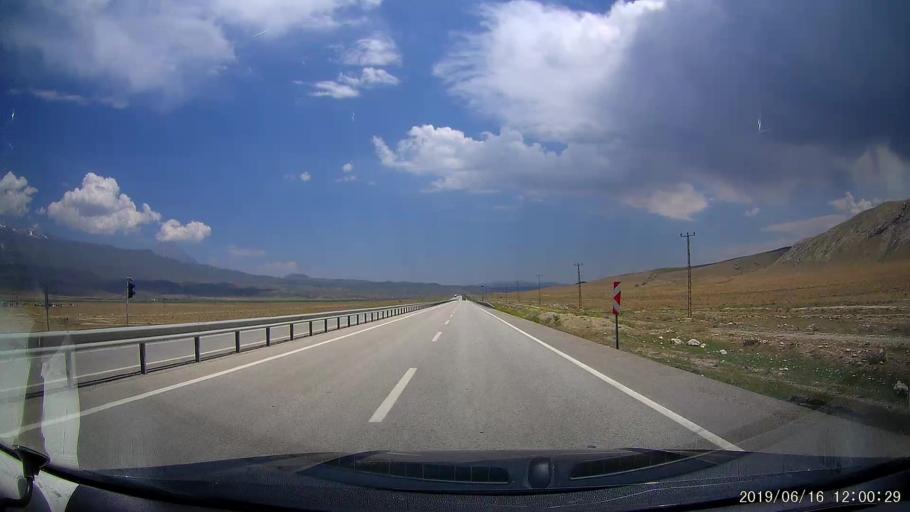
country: TR
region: Agri
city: Dogubayazit
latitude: 39.5568
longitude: 44.1729
